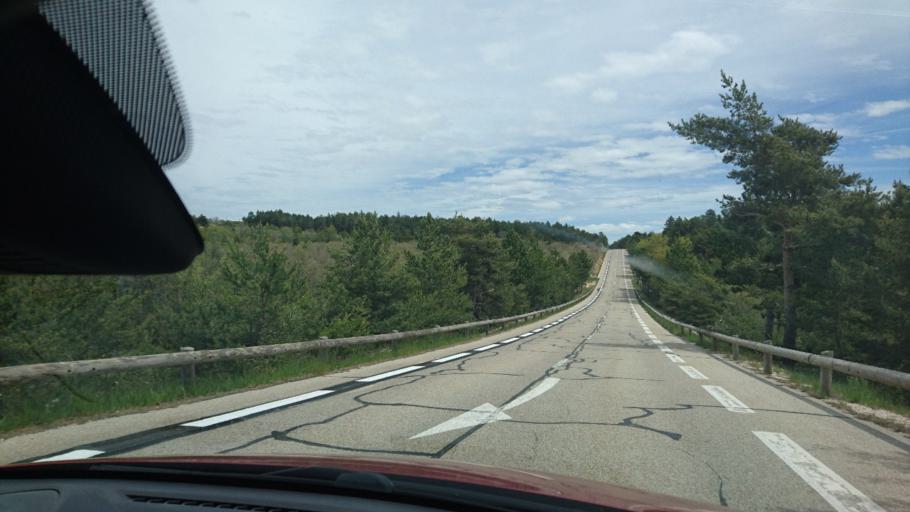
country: FR
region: Provence-Alpes-Cote d'Azur
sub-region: Departement du Vaucluse
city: Sault
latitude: 44.0925
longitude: 5.3336
